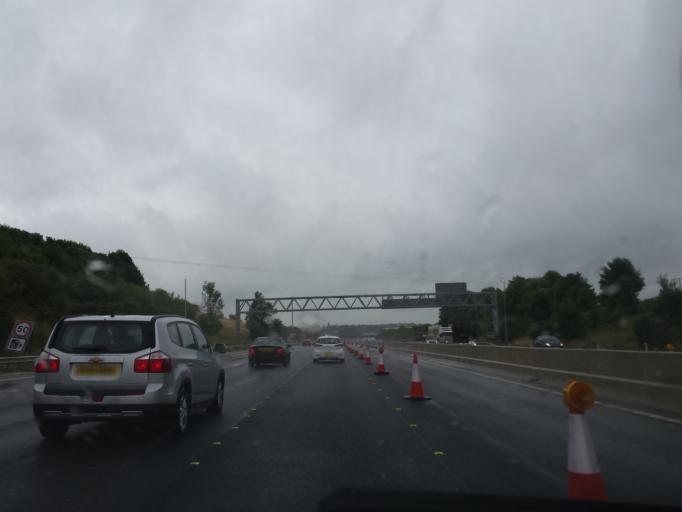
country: GB
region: England
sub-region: Rotherham
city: Wales
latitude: 53.3570
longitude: -1.2847
